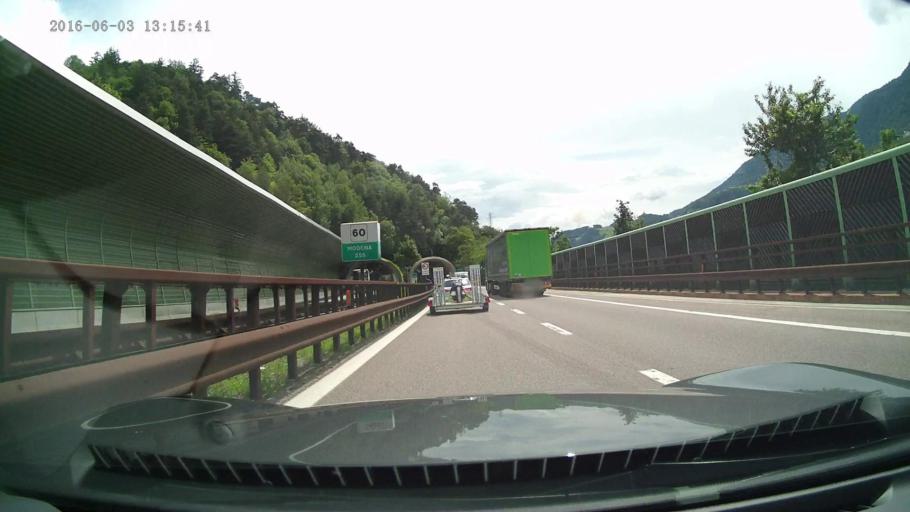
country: IT
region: Trentino-Alto Adige
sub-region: Bolzano
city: Ponte Gardena
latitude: 46.6002
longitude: 11.5338
